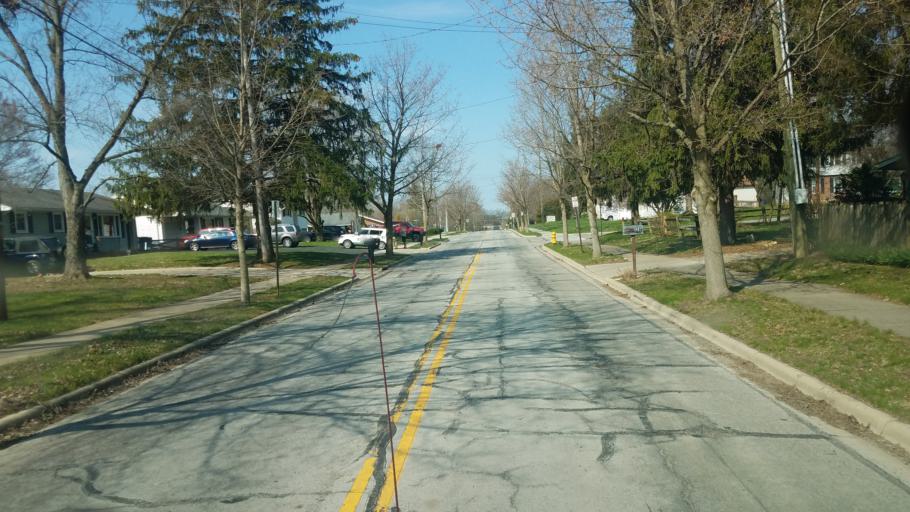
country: US
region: Ohio
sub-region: Delaware County
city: Delaware
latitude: 40.2815
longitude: -83.0733
